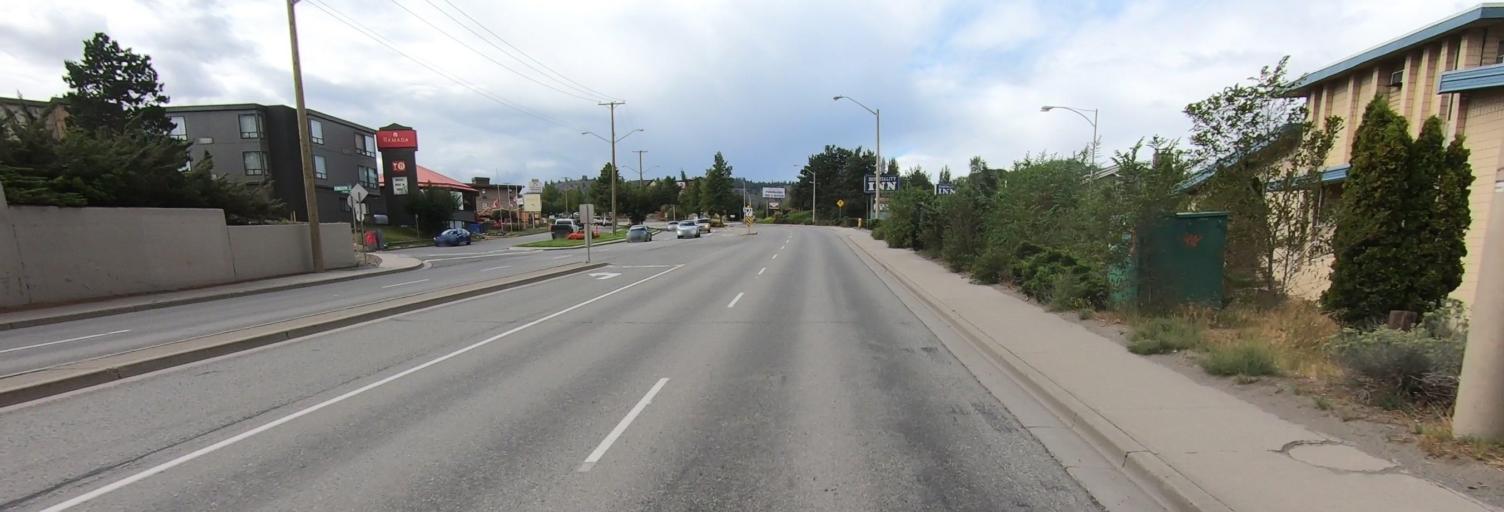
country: CA
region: British Columbia
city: Kamloops
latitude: 50.6736
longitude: -120.3511
